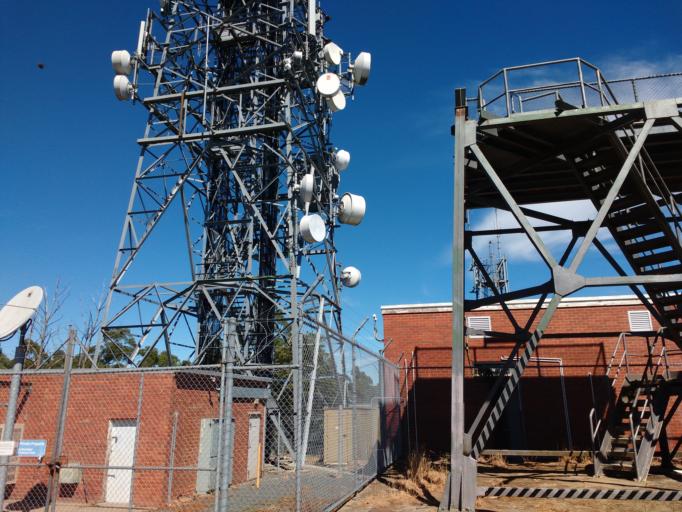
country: AU
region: Victoria
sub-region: Yarra Ranges
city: Healesville
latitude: -37.5674
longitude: 145.5255
